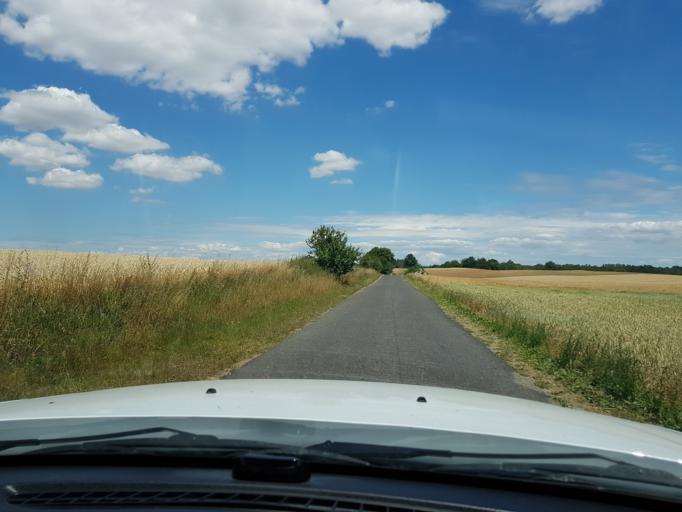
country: PL
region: West Pomeranian Voivodeship
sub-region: Powiat mysliborski
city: Barlinek
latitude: 52.9674
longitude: 15.1243
